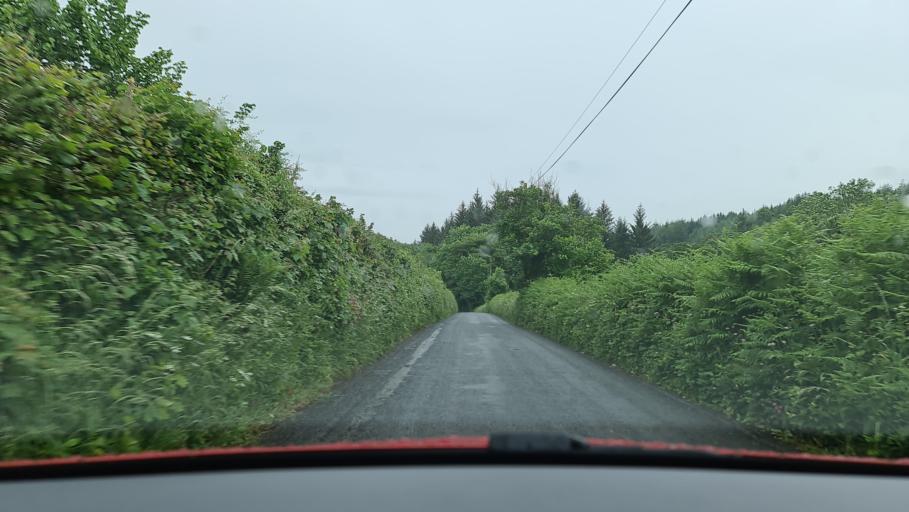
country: GB
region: England
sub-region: Cornwall
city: Liskeard
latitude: 50.4625
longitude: -4.5574
